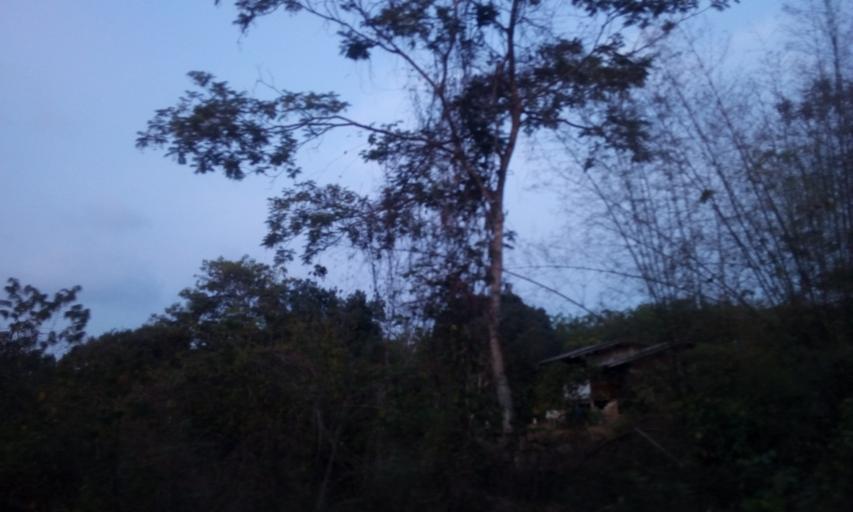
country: TH
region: Trat
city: Laem Ngop
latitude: 12.2126
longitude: 102.2930
